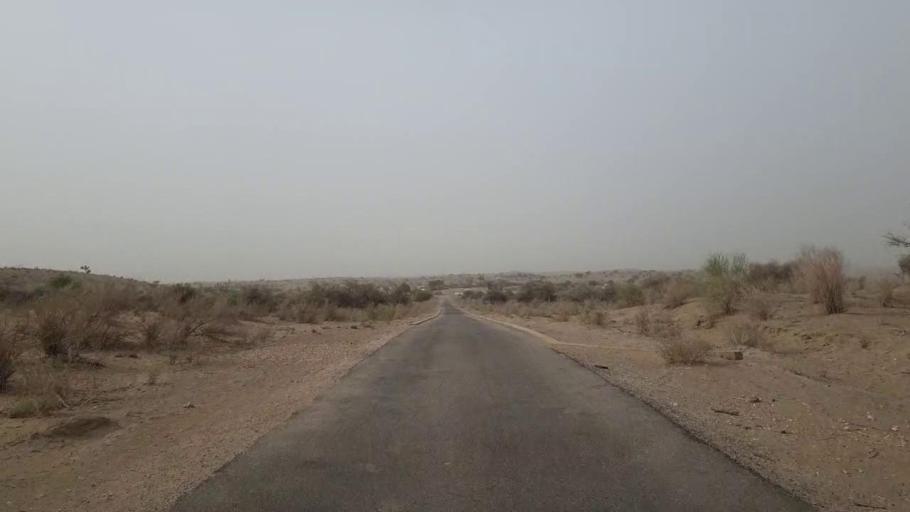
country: PK
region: Sindh
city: Islamkot
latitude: 24.5698
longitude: 70.3642
